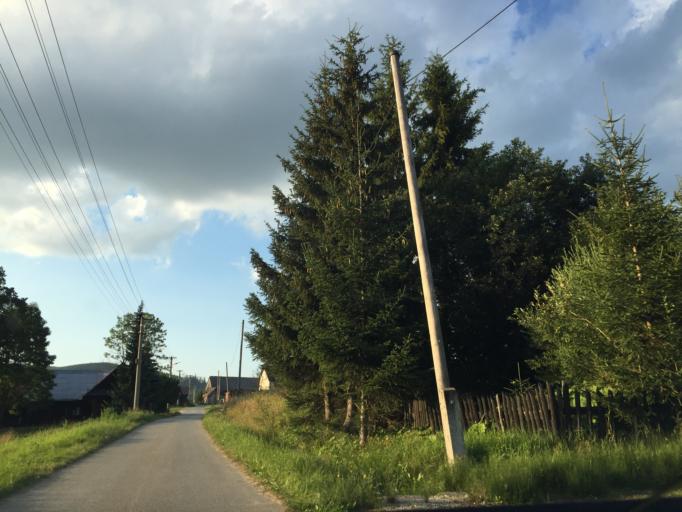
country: PL
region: Silesian Voivodeship
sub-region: Powiat zywiecki
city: Korbielow
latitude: 49.4866
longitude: 19.3816
